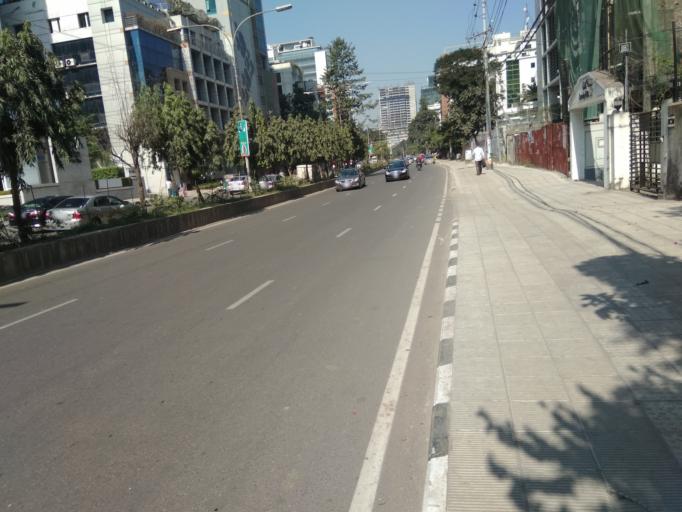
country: BD
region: Dhaka
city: Paltan
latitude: 23.7867
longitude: 90.4170
